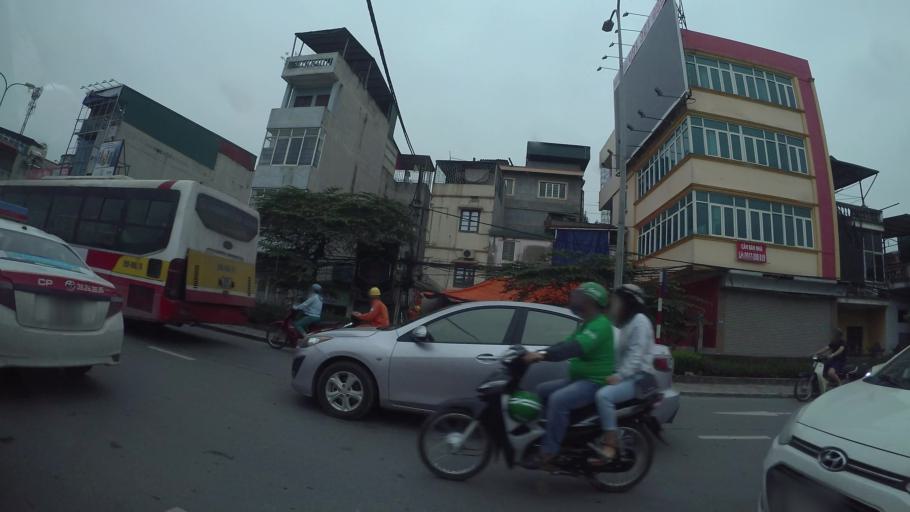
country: VN
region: Ha Noi
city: Hai BaTrung
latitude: 21.0081
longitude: 105.8665
